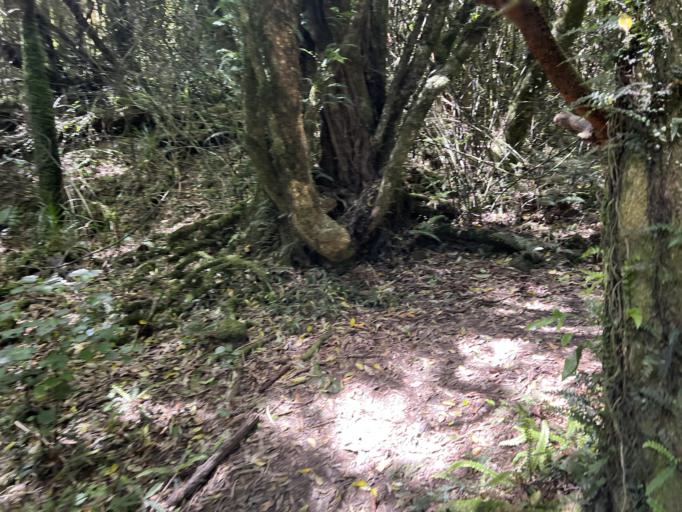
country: NZ
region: Wellington
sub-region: Kapiti Coast District
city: Paraparaumu
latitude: -40.8806
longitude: 175.0897
